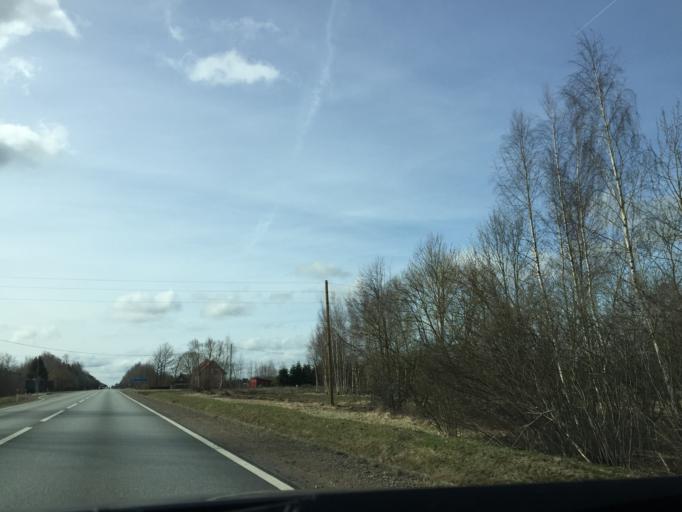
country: LV
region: Jelgava
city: Jelgava
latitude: 56.5313
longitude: 23.7059
